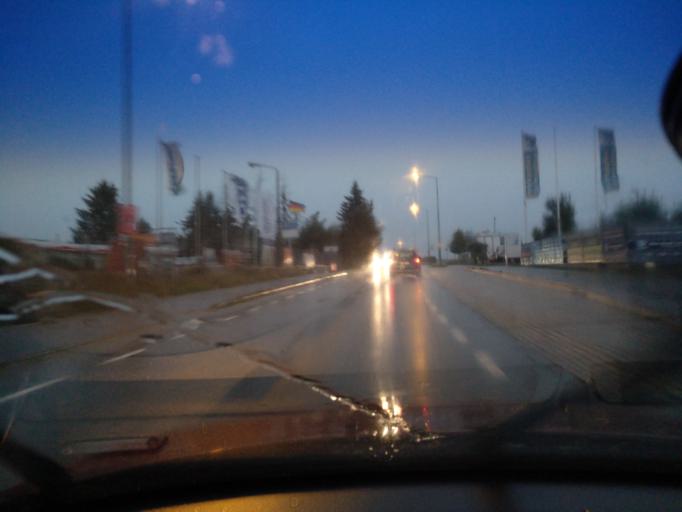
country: DE
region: Saxony
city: Bautzen
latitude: 51.1810
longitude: 14.4151
